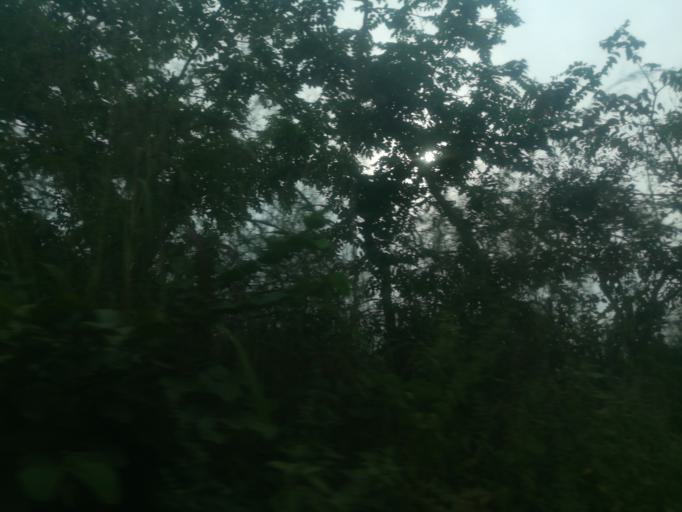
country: NG
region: Ogun
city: Ayetoro
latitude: 7.2529
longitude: 3.1164
